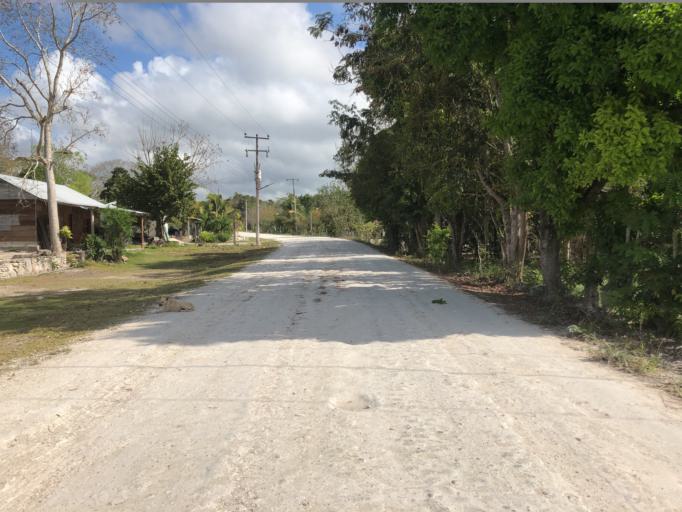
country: MX
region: Quintana Roo
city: Nicolas Bravo
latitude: 18.4545
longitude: -89.3058
